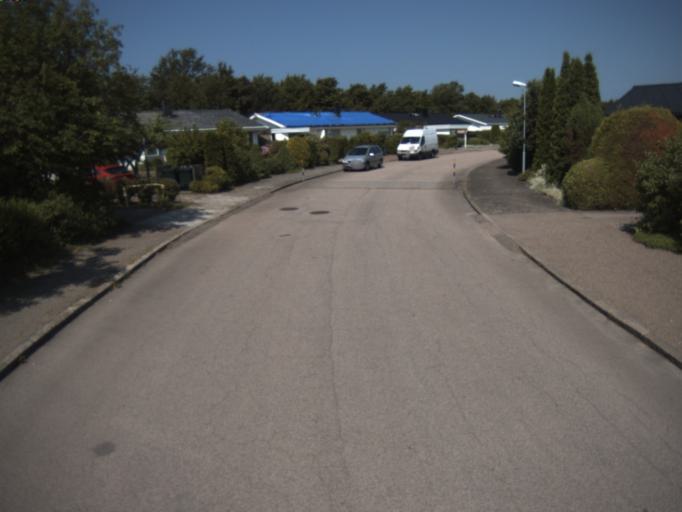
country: SE
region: Skane
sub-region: Helsingborg
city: Helsingborg
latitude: 56.0507
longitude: 12.7366
